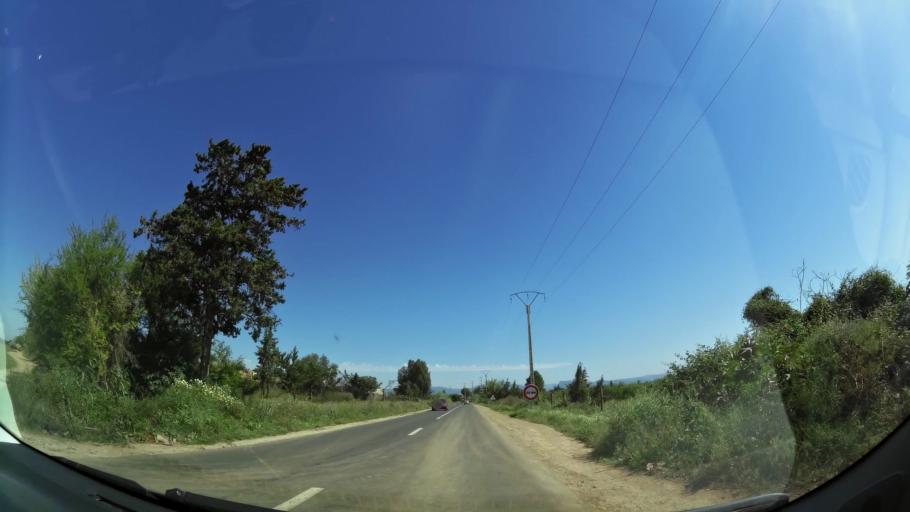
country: MA
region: Oriental
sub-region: Berkane-Taourirt
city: Madagh
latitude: 35.0198
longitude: -2.4079
